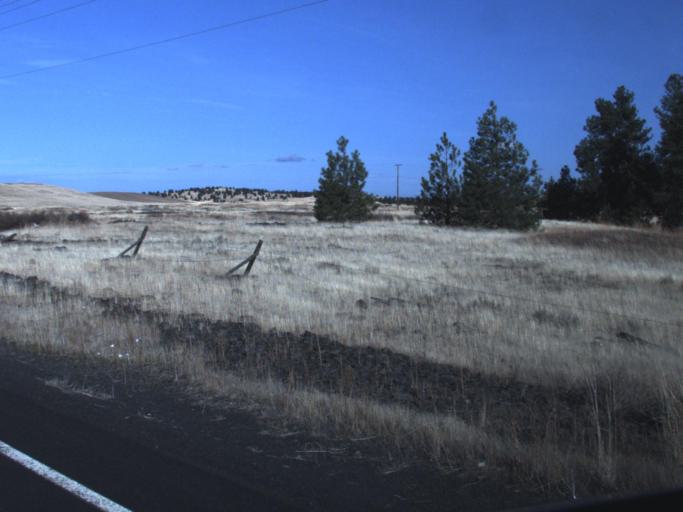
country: US
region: Washington
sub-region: Lincoln County
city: Davenport
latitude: 47.7581
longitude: -118.1735
